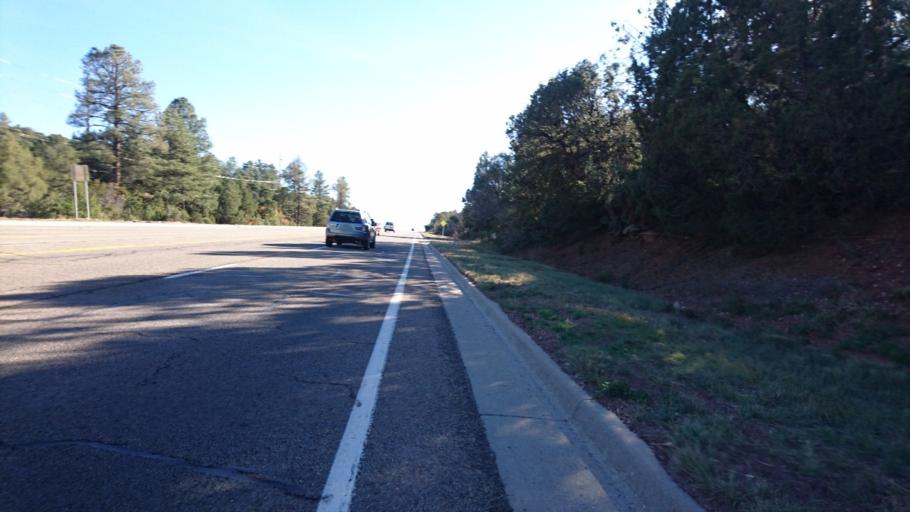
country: US
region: New Mexico
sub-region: Bernalillo County
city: Sandia Knolls
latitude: 35.1519
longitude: -106.3580
